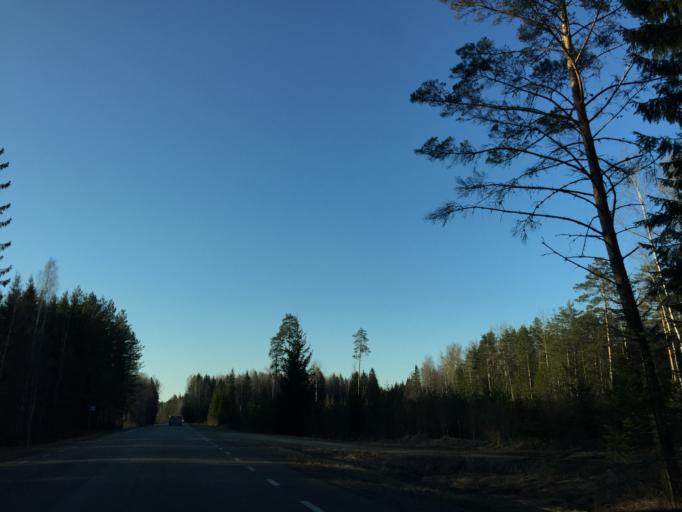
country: EE
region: Ida-Virumaa
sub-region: Toila vald
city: Voka
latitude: 59.1497
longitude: 27.6083
